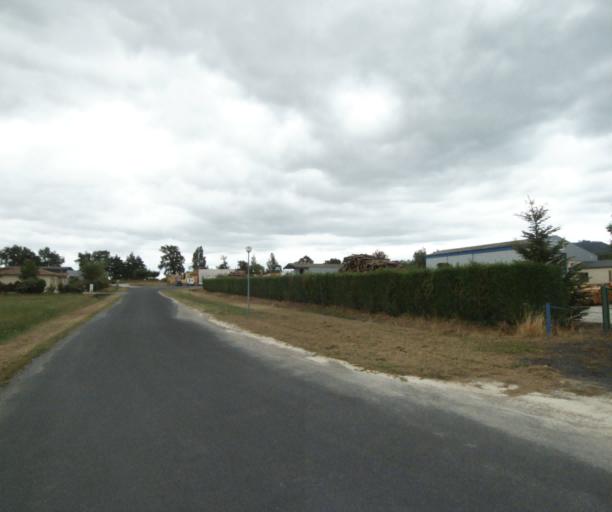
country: FR
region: Midi-Pyrenees
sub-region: Departement du Tarn
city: Soreze
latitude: 43.4555
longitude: 2.0472
